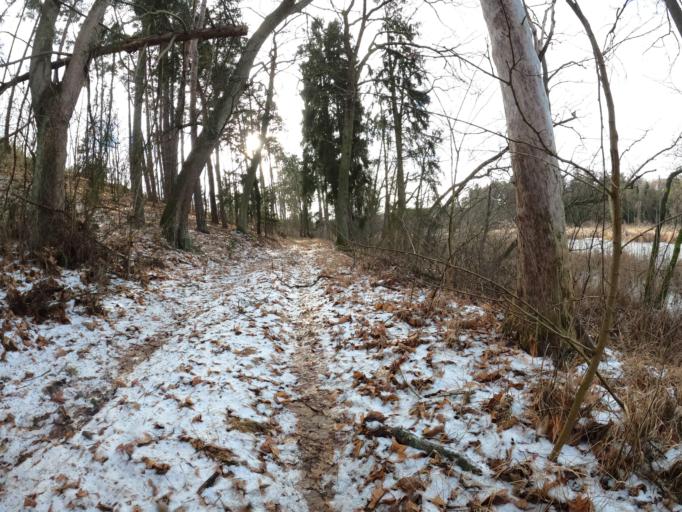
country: PL
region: Lubusz
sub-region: Powiat slubicki
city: Cybinka
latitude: 52.2638
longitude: 14.7926
